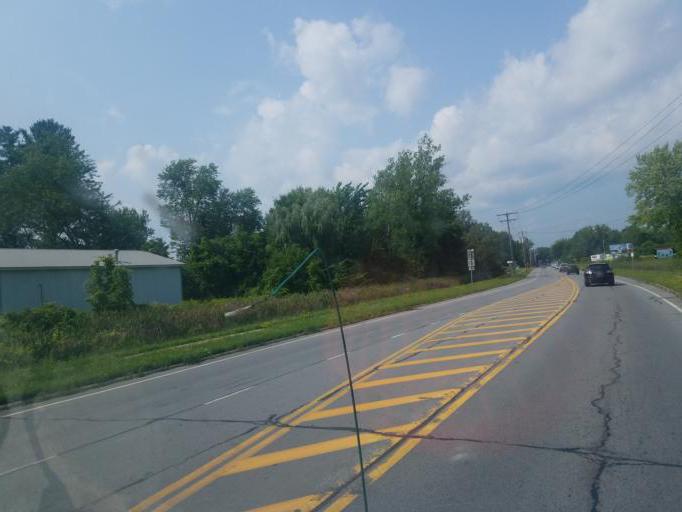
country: US
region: New York
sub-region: Fulton County
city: Johnstown
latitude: 43.0021
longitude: -74.3579
